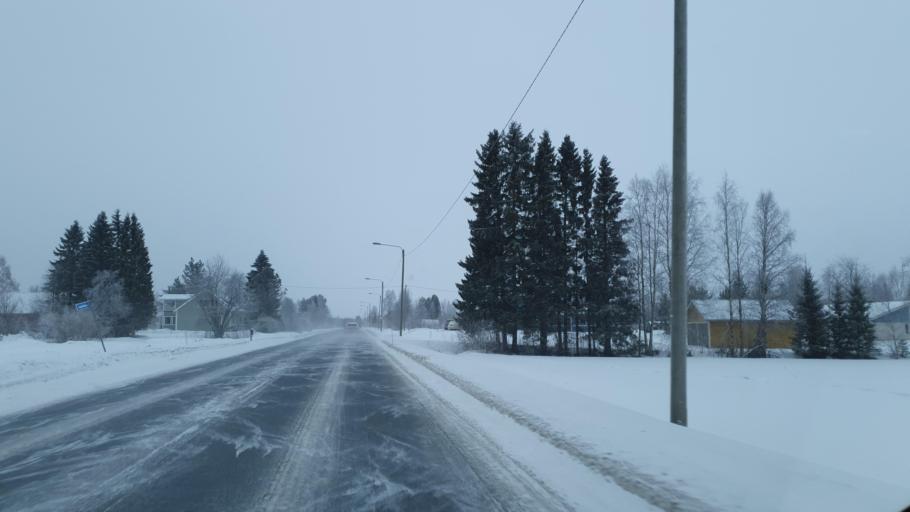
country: FI
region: Lapland
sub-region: Torniolaakso
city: Ylitornio
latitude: 66.1371
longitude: 23.9426
